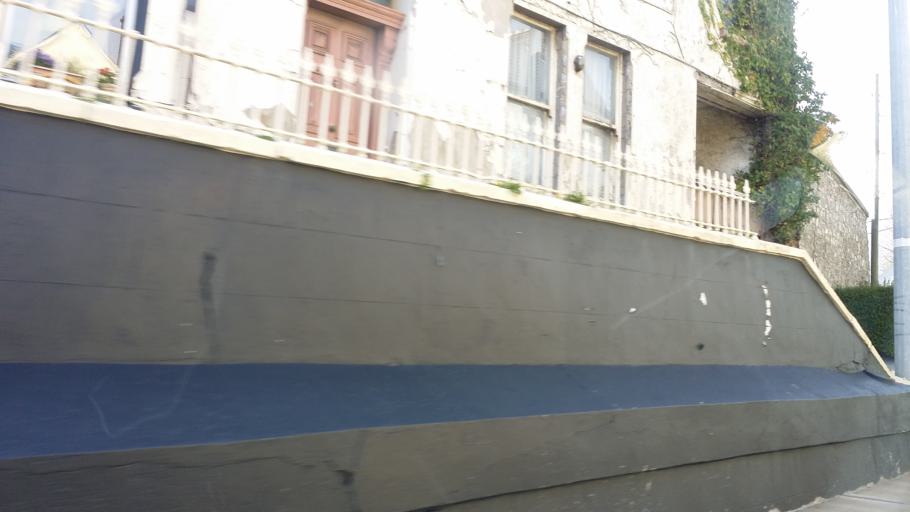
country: IE
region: Ulster
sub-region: County Donegal
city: Ballyshannon
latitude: 54.5033
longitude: -8.1922
